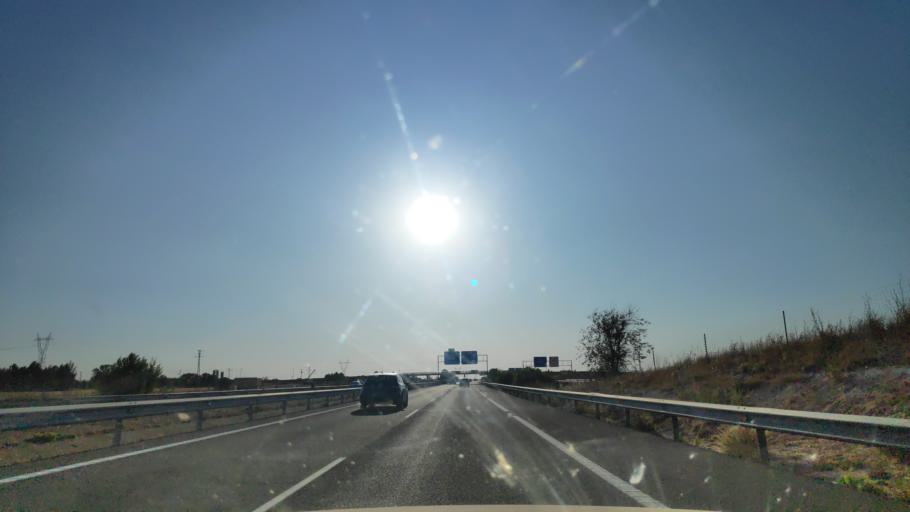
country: ES
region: Castille-La Mancha
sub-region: Provincia de Cuenca
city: Tarancon
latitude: 39.9938
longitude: -3.0027
